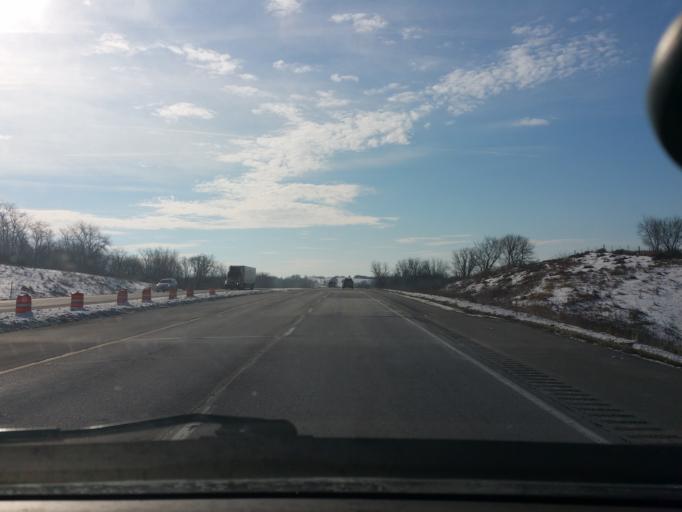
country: US
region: Iowa
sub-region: Warren County
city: Norwalk
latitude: 41.3344
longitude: -93.7799
